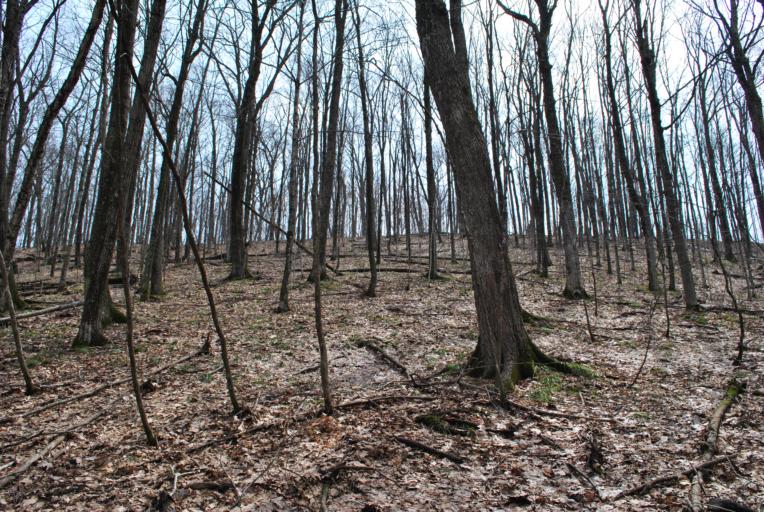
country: US
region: Wisconsin
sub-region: Dunn County
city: Boyceville
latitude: 44.9263
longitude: -92.0850
